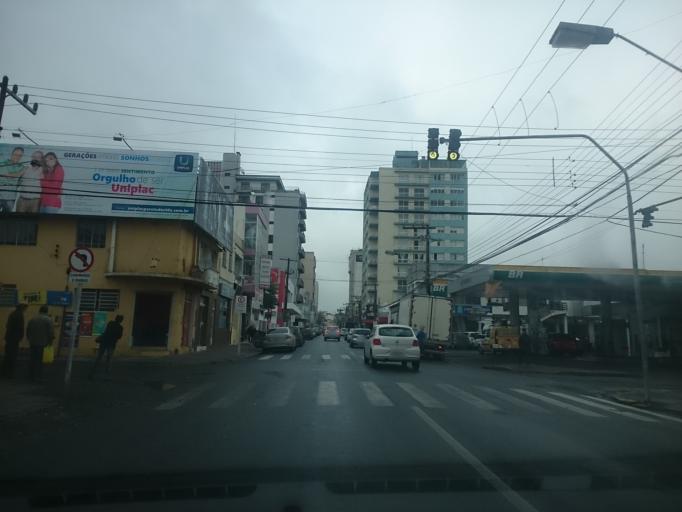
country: BR
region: Santa Catarina
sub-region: Lages
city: Lages
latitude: -27.8126
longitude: -50.3249
